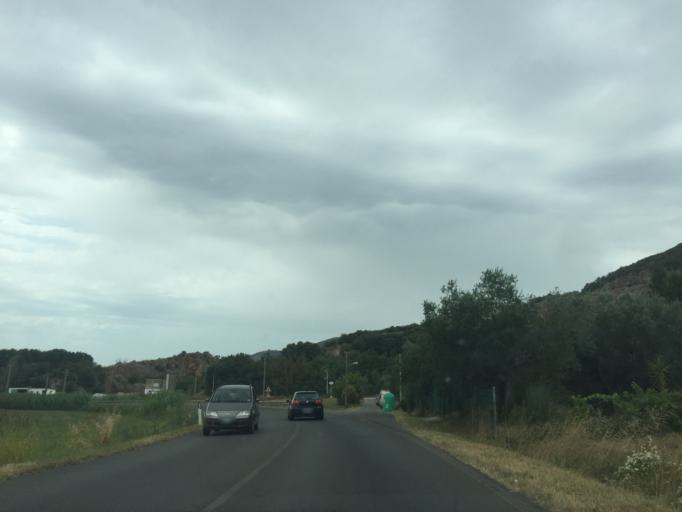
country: IT
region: Tuscany
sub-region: Province of Pisa
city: Asciano
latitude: 43.7348
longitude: 10.4772
